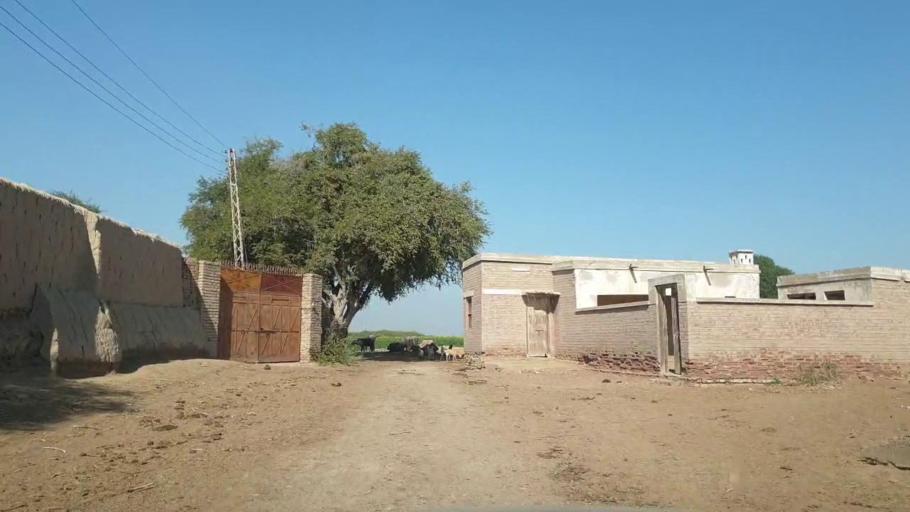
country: PK
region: Sindh
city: Tando Adam
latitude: 25.6574
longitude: 68.6826
